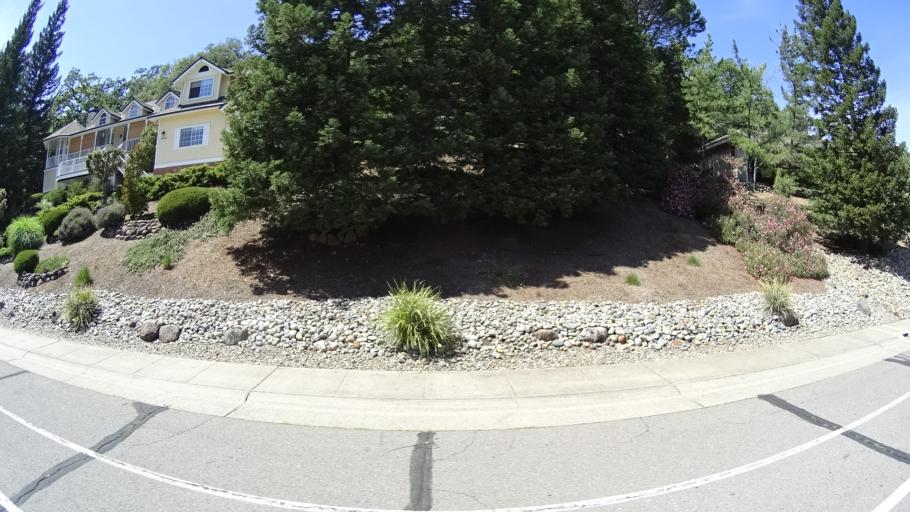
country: US
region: California
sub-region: Placer County
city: Rocklin
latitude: 38.8155
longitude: -121.2371
